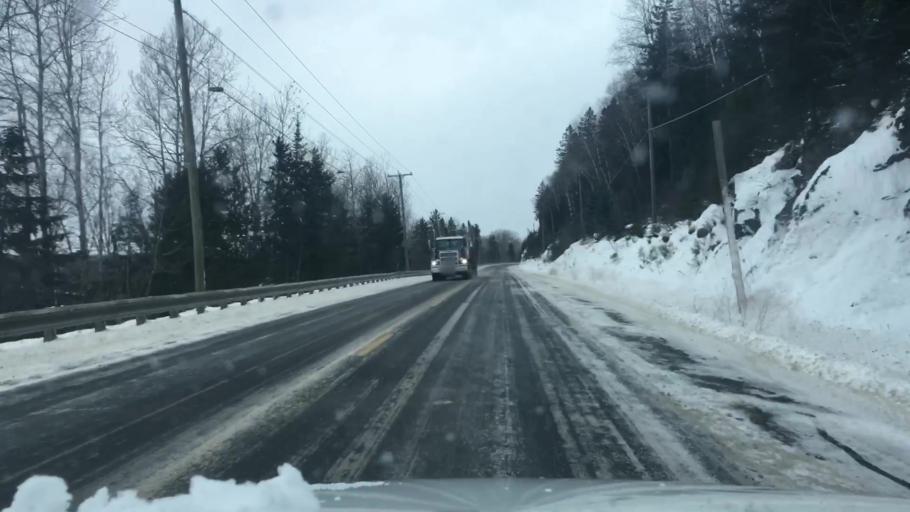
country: US
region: Maine
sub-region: Aroostook County
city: Madawaska
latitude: 47.3287
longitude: -68.1876
